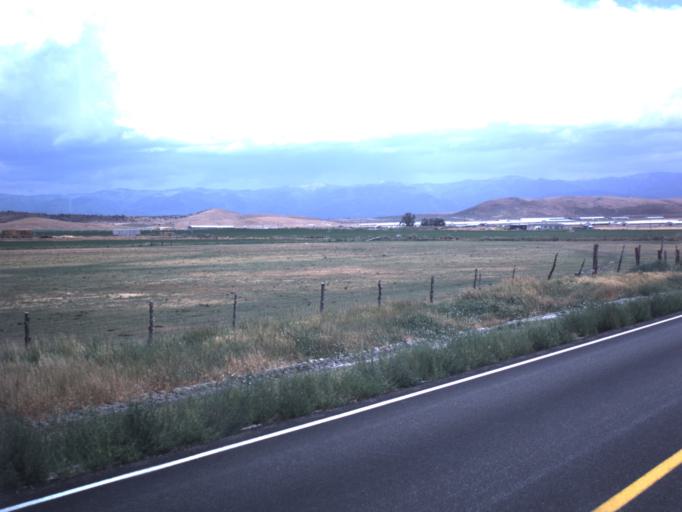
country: US
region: Utah
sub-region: Sanpete County
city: Moroni
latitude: 39.5732
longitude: -111.6084
